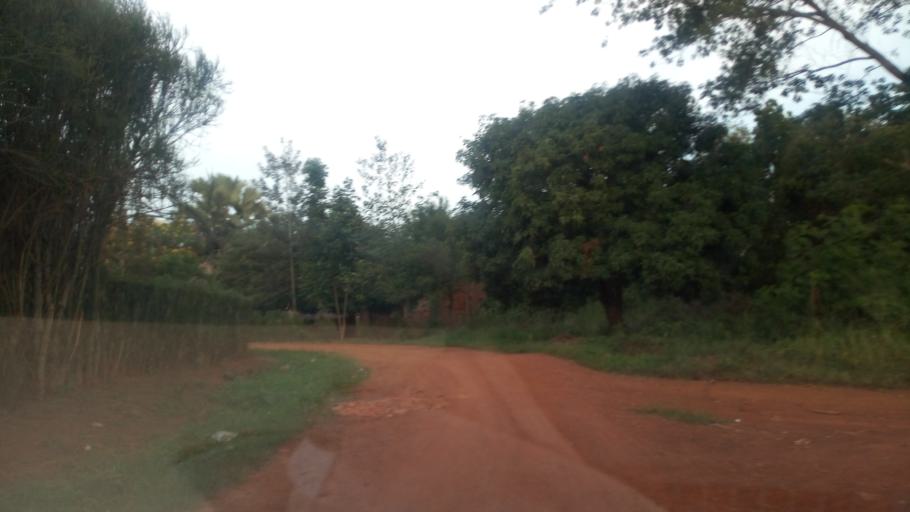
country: UG
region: Western Region
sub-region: Kiryandongo District
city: Kiryandongo
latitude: 1.8006
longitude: 32.0076
